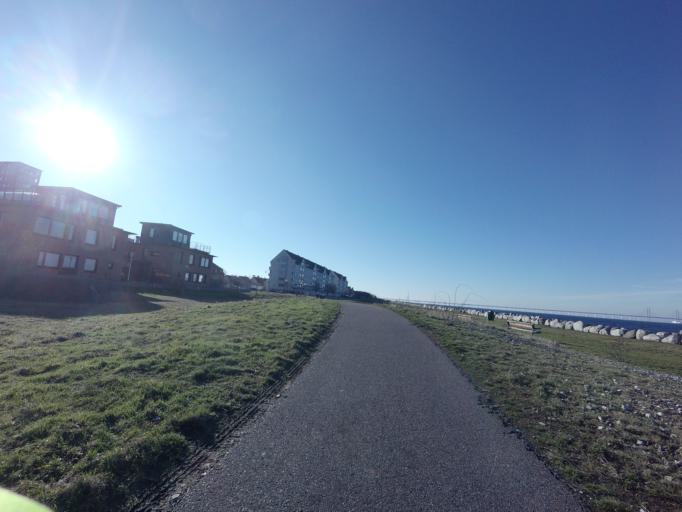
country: SE
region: Skane
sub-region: Malmo
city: Bunkeflostrand
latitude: 55.5915
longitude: 12.9201
